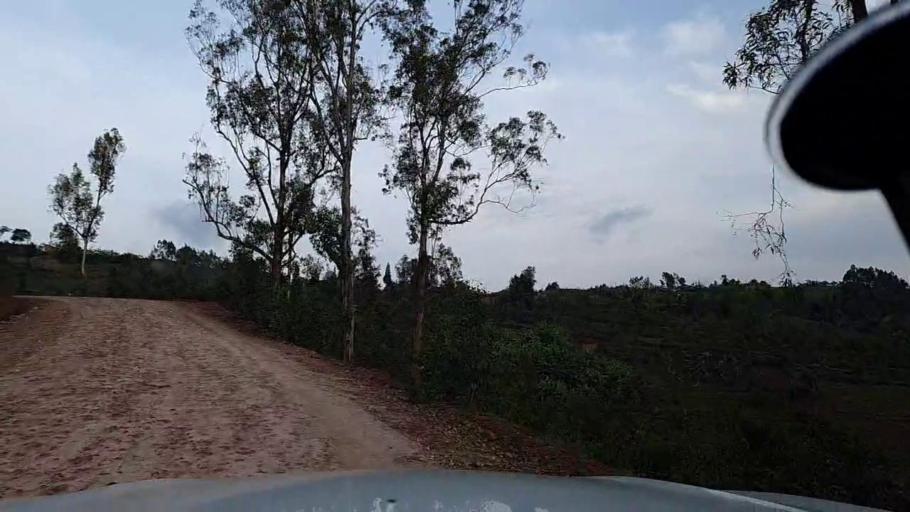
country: RW
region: Southern Province
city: Nyanza
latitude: -2.2124
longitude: 29.6312
